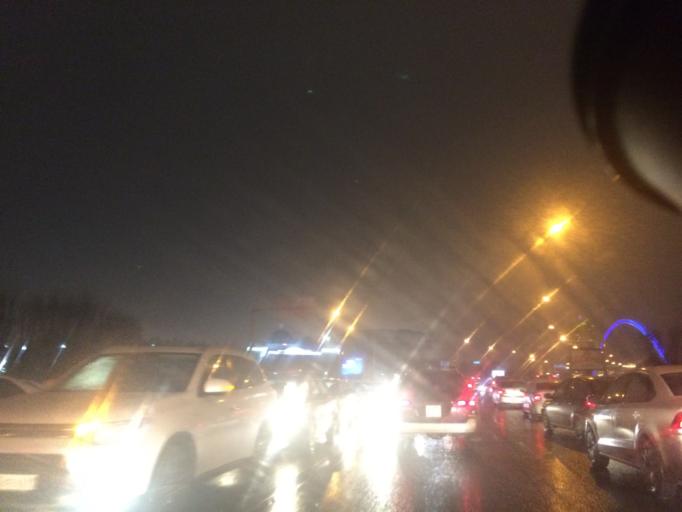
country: KZ
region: Astana Qalasy
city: Astana
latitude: 51.1477
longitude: 71.4230
